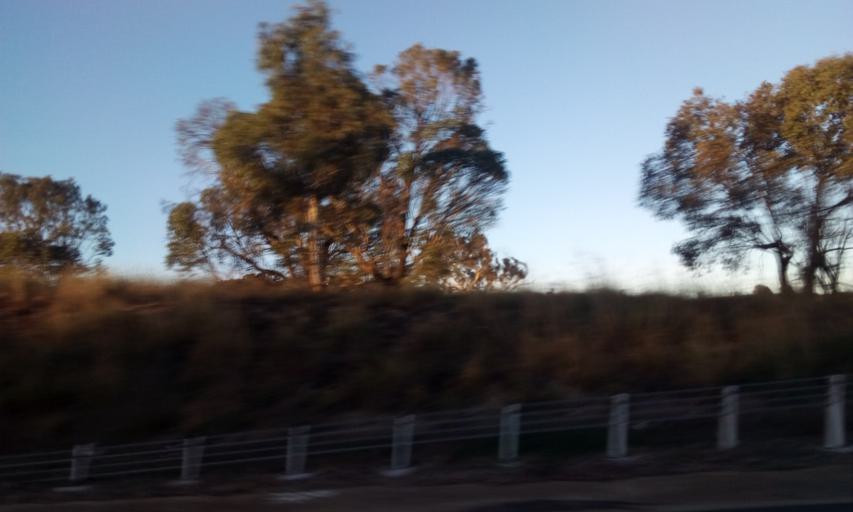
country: AU
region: New South Wales
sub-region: Goulburn Mulwaree
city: Goulburn
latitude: -34.7887
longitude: 149.6454
